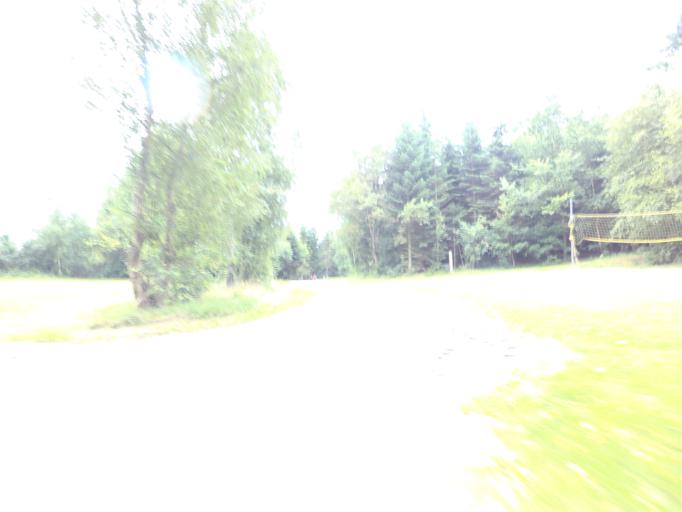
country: DK
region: Central Jutland
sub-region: Silkeborg Kommune
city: Virklund
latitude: 56.0328
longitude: 9.4831
